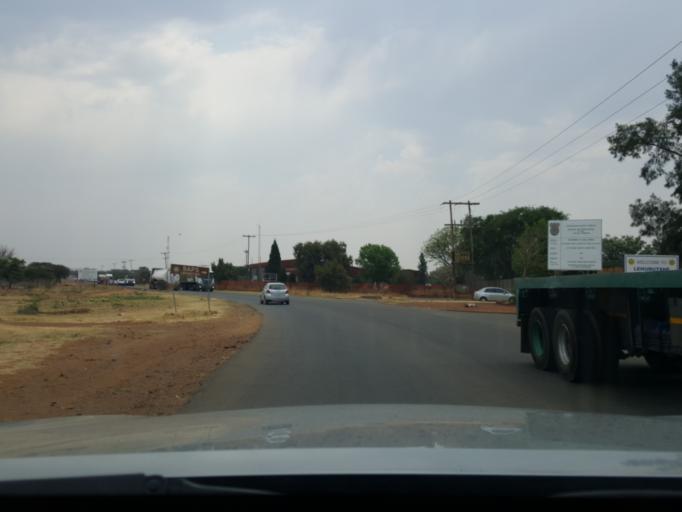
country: ZA
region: North-West
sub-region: Ngaka Modiri Molema District Municipality
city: Zeerust
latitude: -25.4883
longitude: 25.9842
